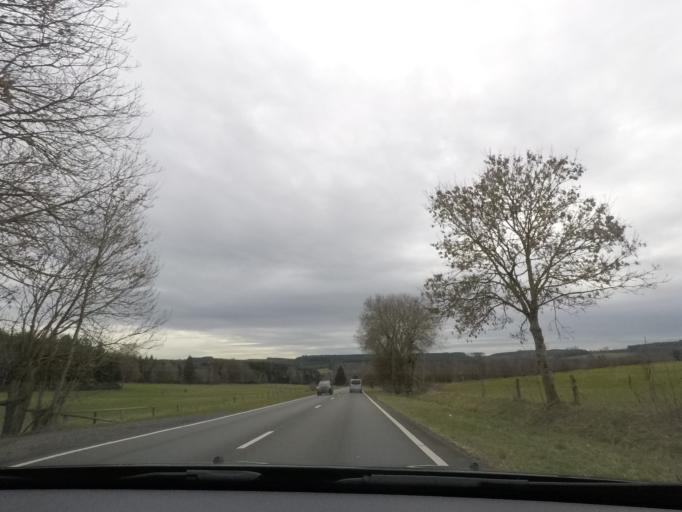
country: BE
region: Wallonia
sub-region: Province du Luxembourg
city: Bastogne
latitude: 49.9869
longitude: 5.7576
